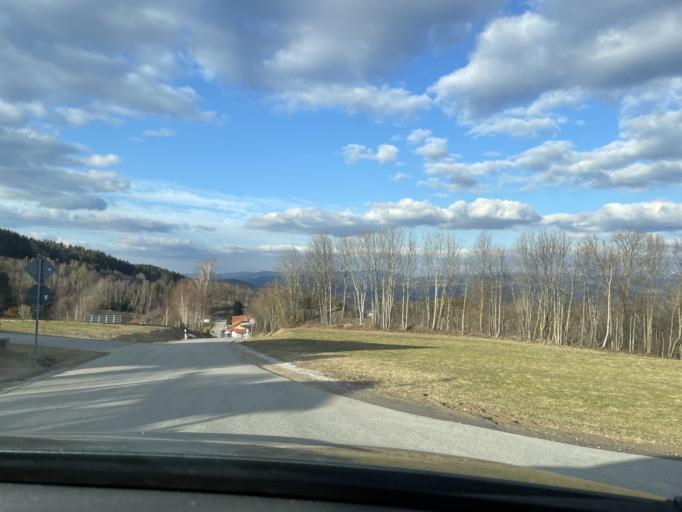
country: DE
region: Bavaria
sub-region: Lower Bavaria
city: Kollnburg
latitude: 49.0255
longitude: 12.8616
